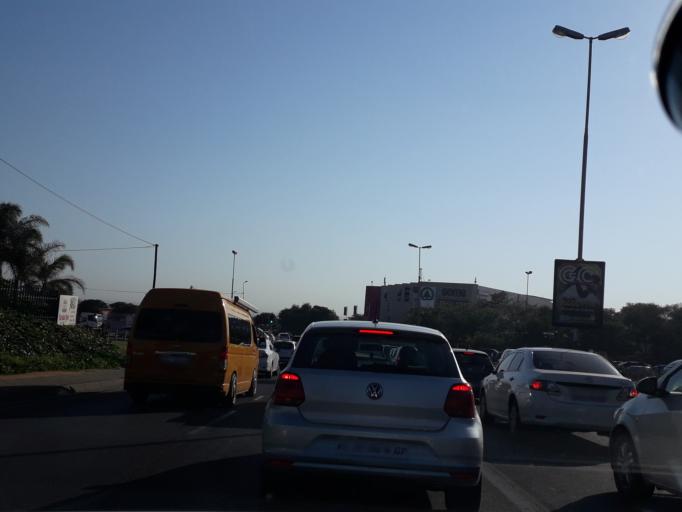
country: ZA
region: Gauteng
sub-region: West Rand District Municipality
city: Muldersdriseloop
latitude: -26.0613
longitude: 27.9548
